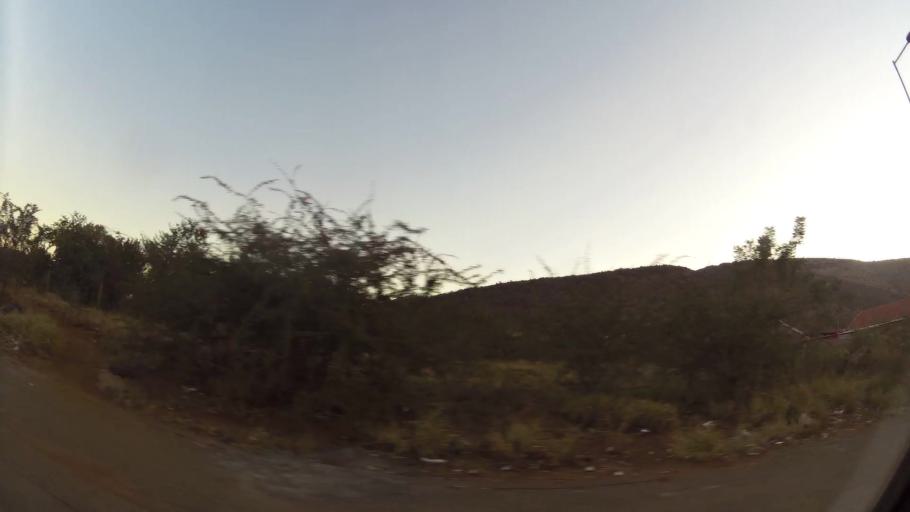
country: ZA
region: North-West
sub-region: Bojanala Platinum District Municipality
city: Rustenburg
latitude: -25.6507
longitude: 27.2014
